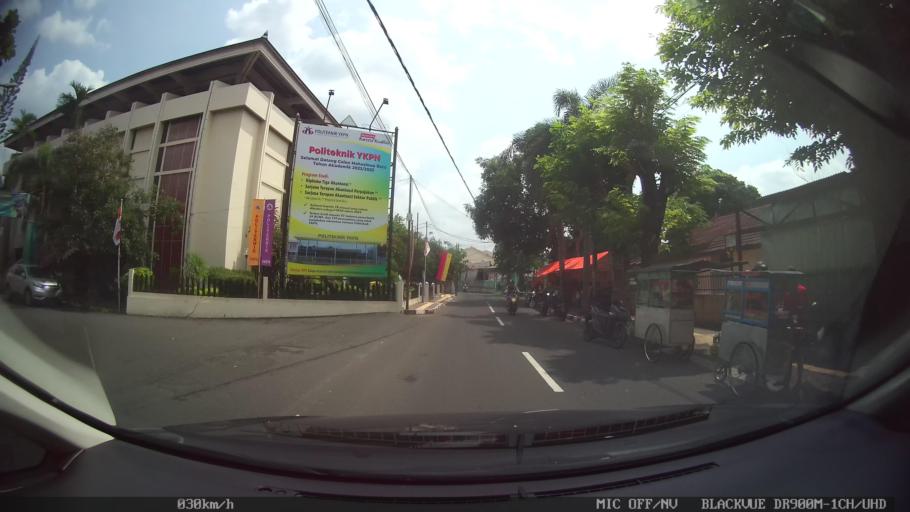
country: ID
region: Daerah Istimewa Yogyakarta
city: Yogyakarta
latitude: -7.7850
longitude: 110.3840
